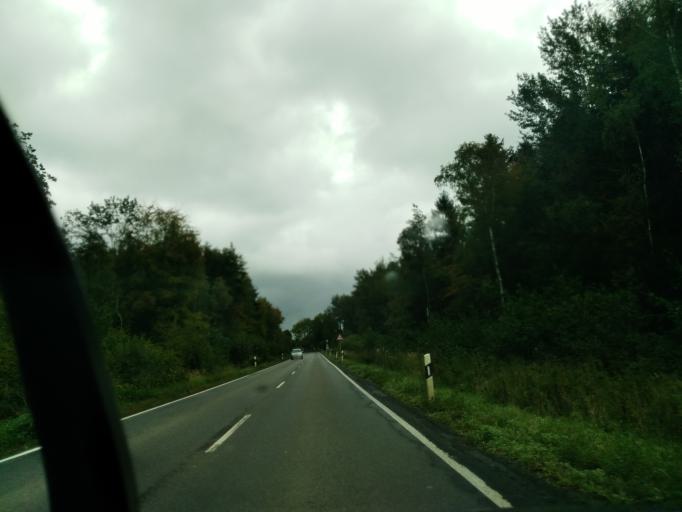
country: DE
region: Rheinland-Pfalz
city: Windhagen
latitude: 50.6577
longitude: 7.3517
